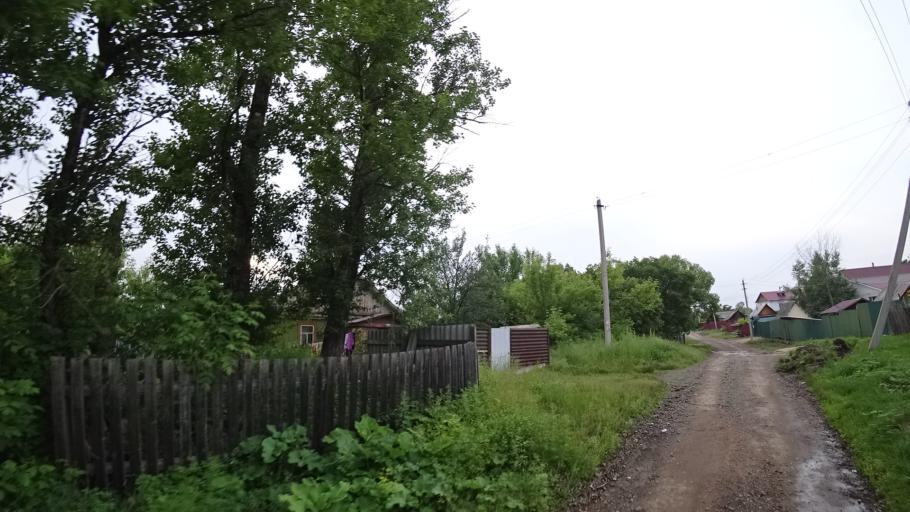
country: RU
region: Primorskiy
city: Novosysoyevka
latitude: 44.2242
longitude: 133.3543
